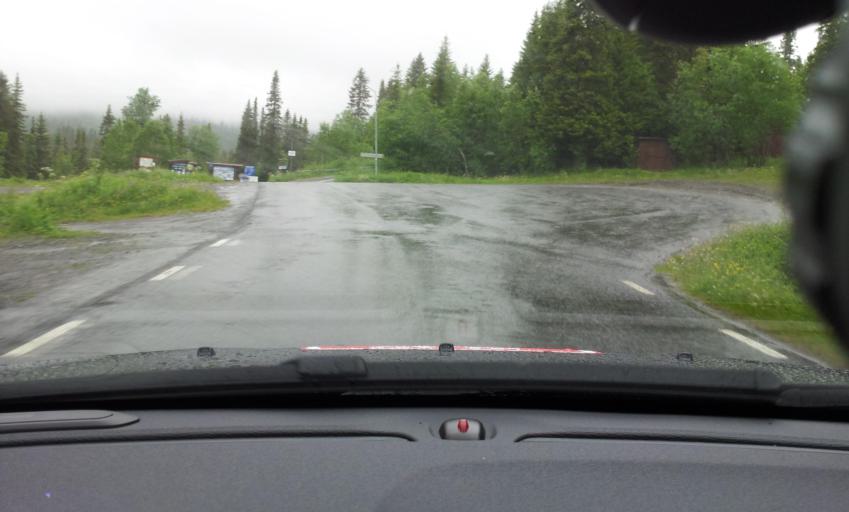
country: SE
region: Jaemtland
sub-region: Are Kommun
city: Are
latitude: 63.3152
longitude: 13.0611
